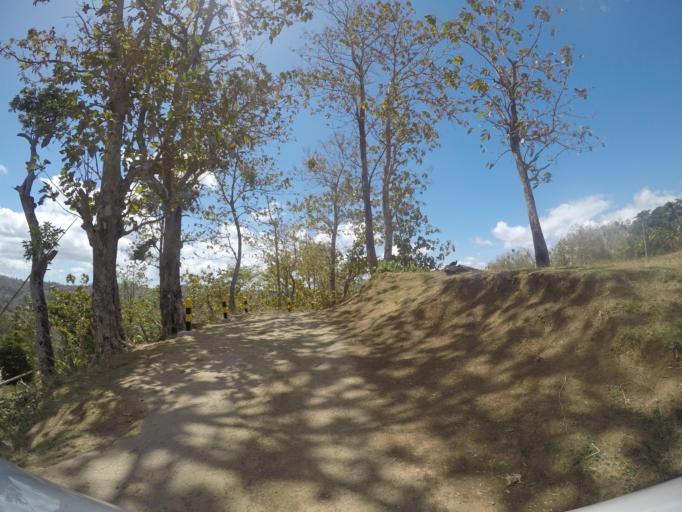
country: TL
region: Lautem
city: Lospalos
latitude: -8.5352
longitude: 126.7984
